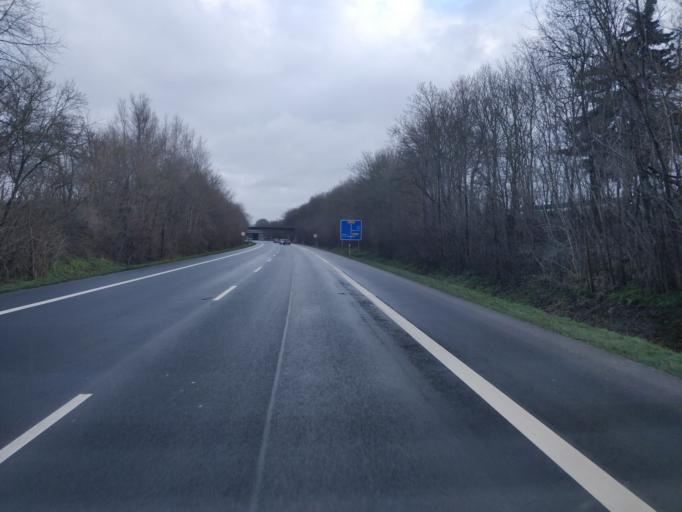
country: DE
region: North Rhine-Westphalia
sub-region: Regierungsbezirk Koln
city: Weilerswist
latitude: 50.7129
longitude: 6.8928
